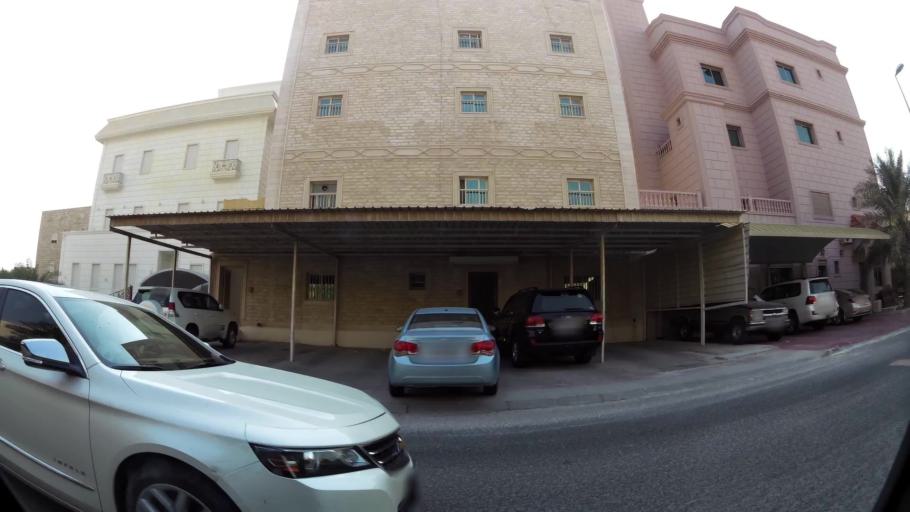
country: KW
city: Al Funaytis
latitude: 29.2205
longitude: 48.0811
